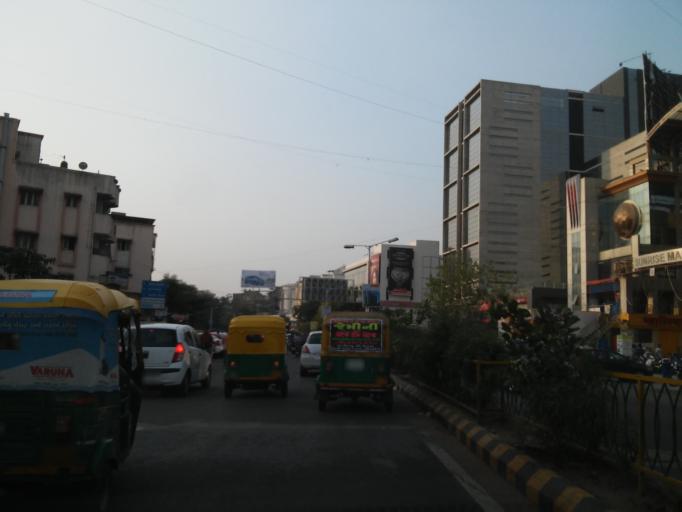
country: IN
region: Gujarat
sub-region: Ahmadabad
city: Sarkhej
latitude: 23.0327
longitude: 72.5247
